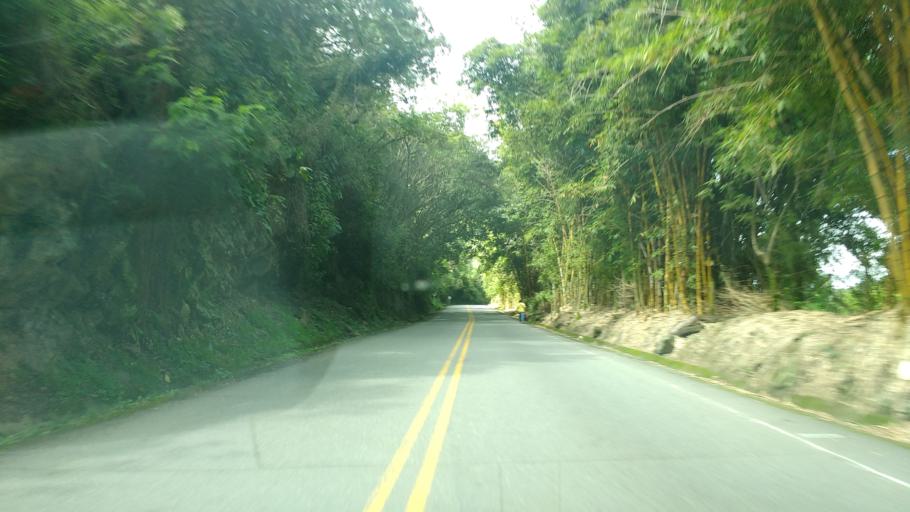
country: CO
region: Antioquia
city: Titiribi
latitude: 6.0295
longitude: -75.7623
